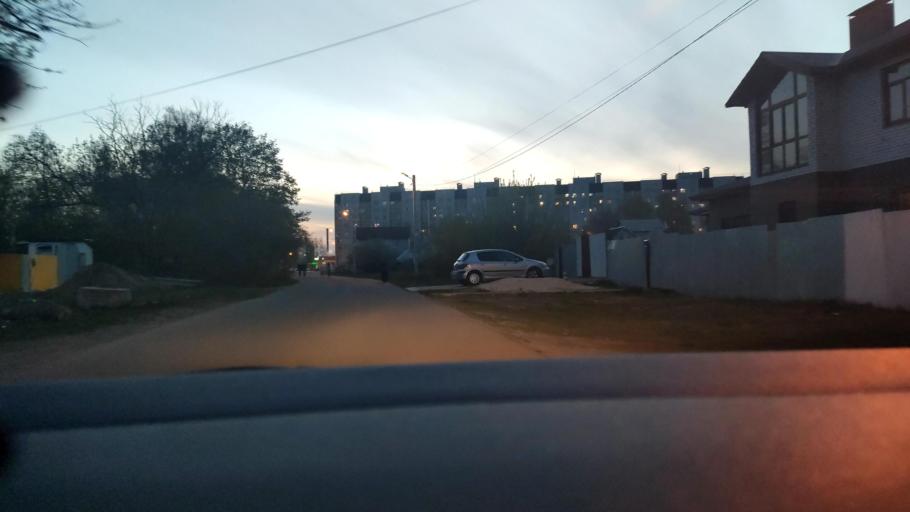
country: RU
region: Voronezj
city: Somovo
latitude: 51.7365
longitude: 39.3214
